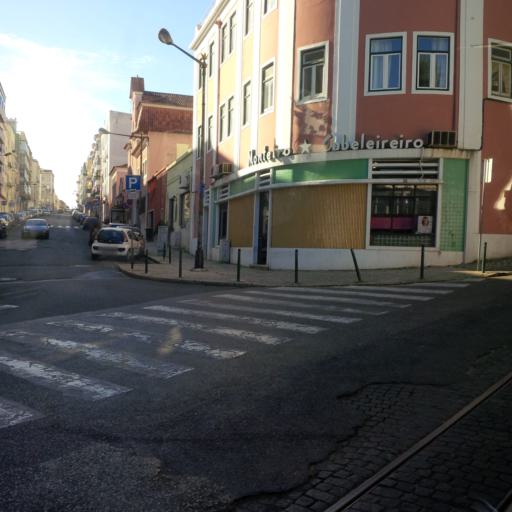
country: PT
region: Lisbon
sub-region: Lisbon
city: Lisbon
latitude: 38.7125
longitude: -9.1561
